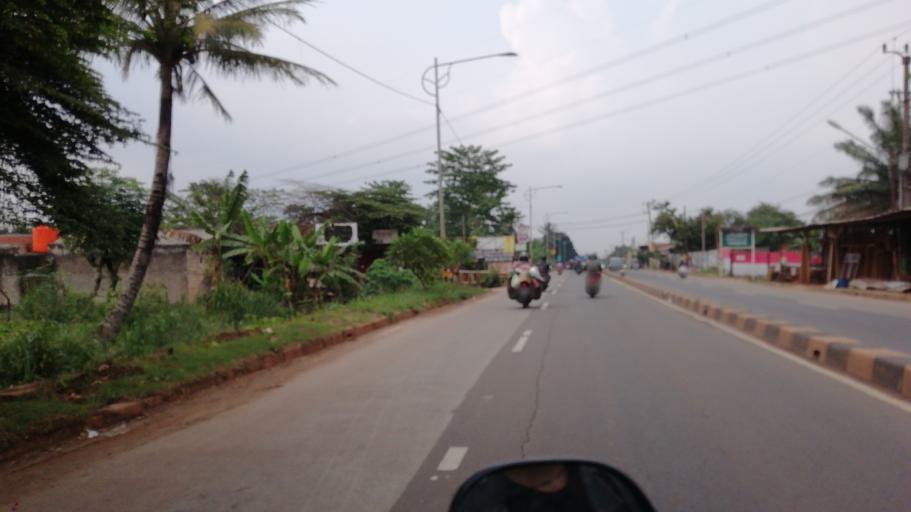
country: ID
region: West Java
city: Parung
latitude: -6.4712
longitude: 106.7292
